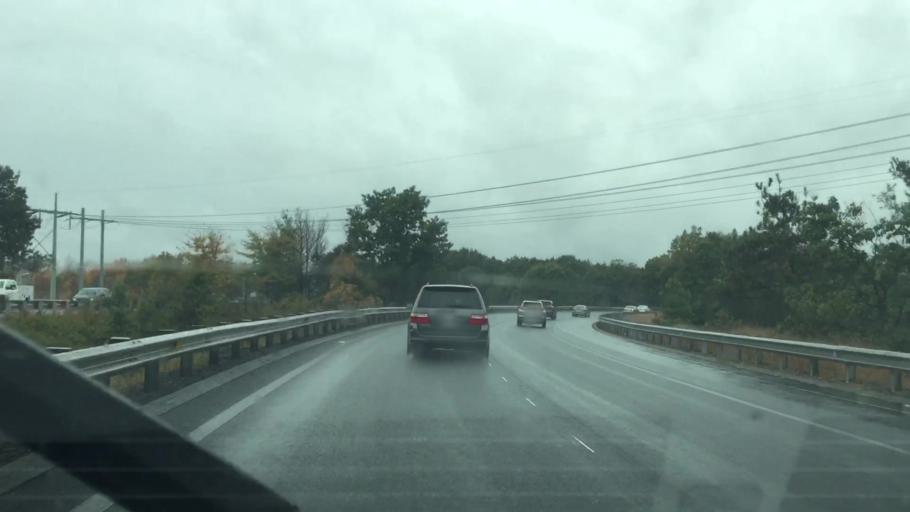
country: US
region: Massachusetts
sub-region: Essex County
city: Methuen
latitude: 42.7320
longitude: -71.1956
